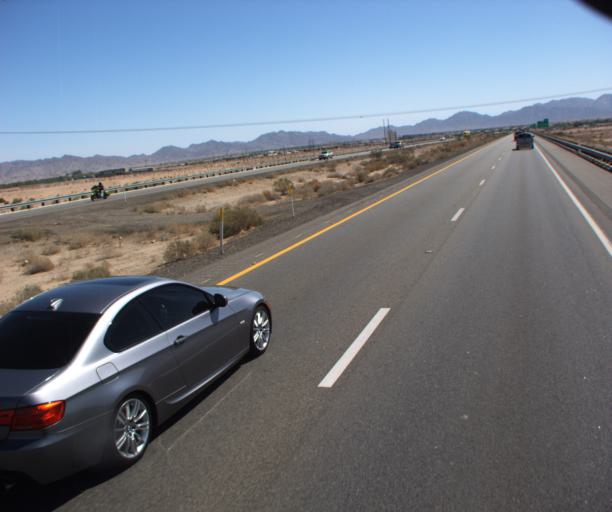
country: US
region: Arizona
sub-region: Yuma County
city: Fortuna Foothills
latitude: 32.6754
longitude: -114.4968
